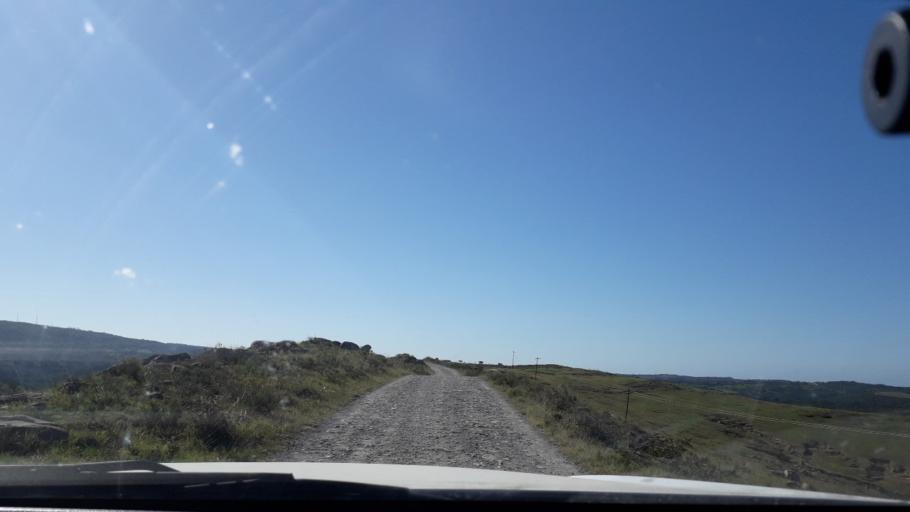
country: ZA
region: Eastern Cape
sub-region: Buffalo City Metropolitan Municipality
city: East London
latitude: -32.8384
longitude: 27.9968
